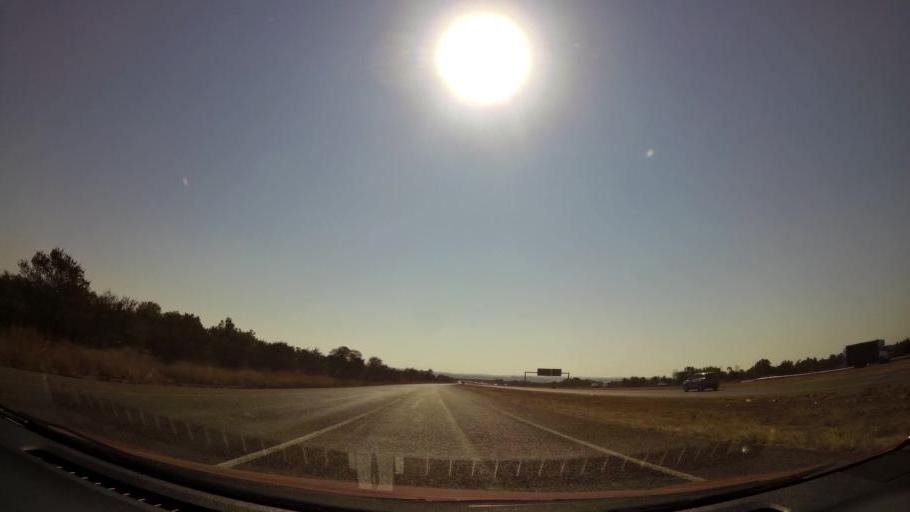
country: ZA
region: North-West
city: Ga-Rankuwa
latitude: -25.6236
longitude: 28.1110
